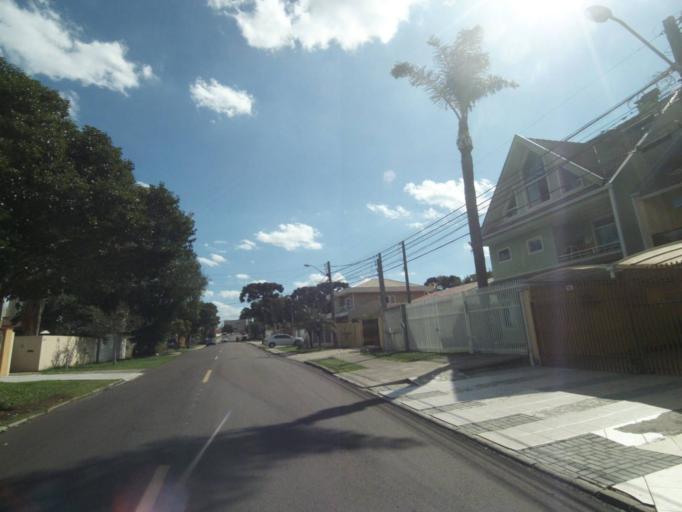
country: BR
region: Parana
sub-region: Curitiba
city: Curitiba
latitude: -25.4354
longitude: -49.3460
